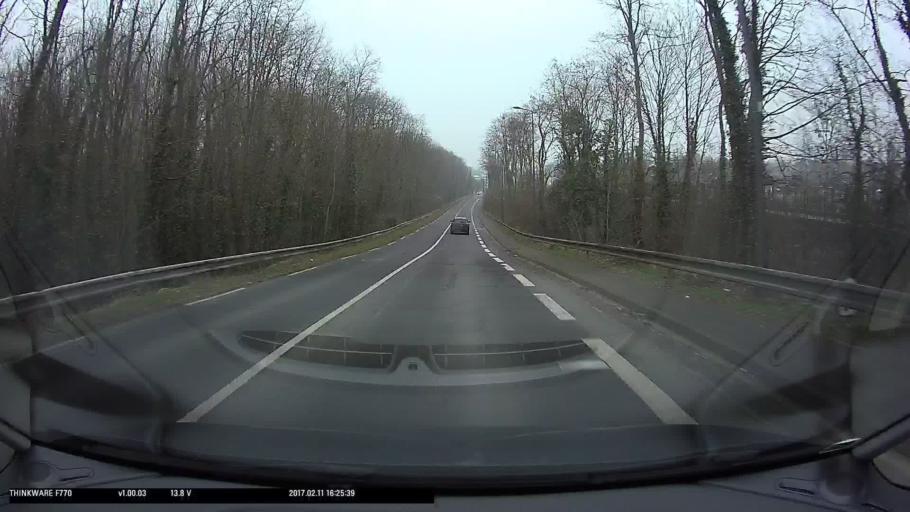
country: FR
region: Ile-de-France
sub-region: Departement du Val-d'Oise
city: Osny
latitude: 49.0631
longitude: 2.0586
